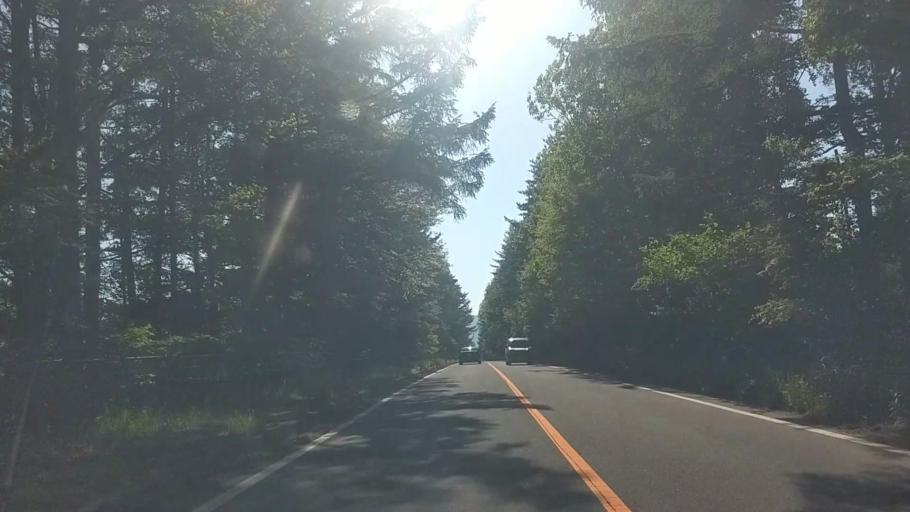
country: JP
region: Nagano
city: Chino
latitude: 35.8989
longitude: 138.3437
